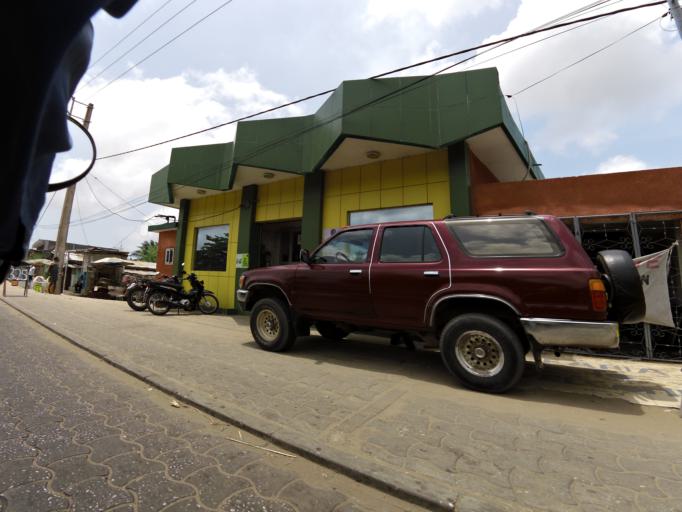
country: BJ
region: Littoral
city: Cotonou
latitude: 6.3863
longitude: 2.3720
